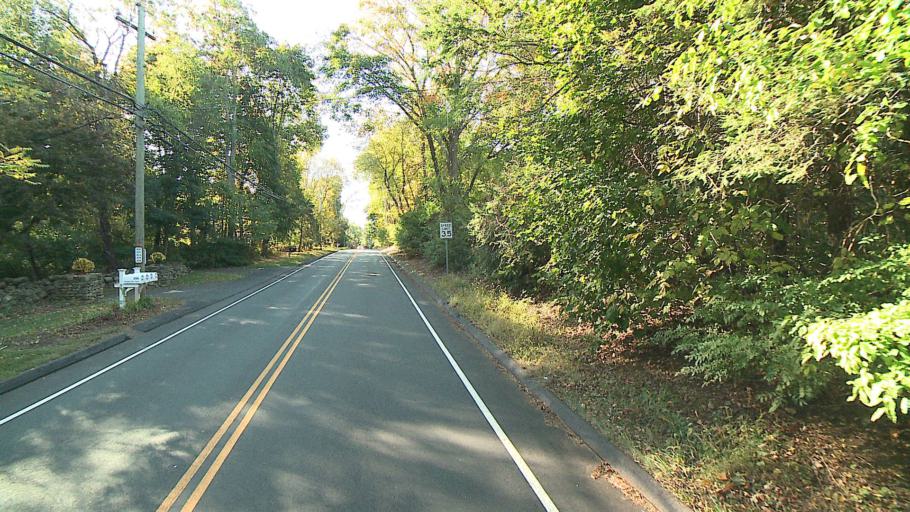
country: US
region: Connecticut
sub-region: Fairfield County
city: Wilton
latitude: 41.1913
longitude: -73.3977
